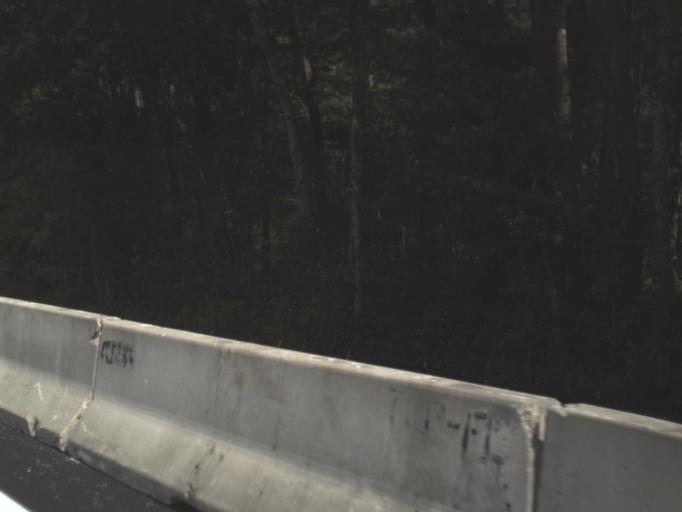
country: US
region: Florida
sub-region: Columbia County
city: Watertown
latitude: 30.2442
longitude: -82.5669
